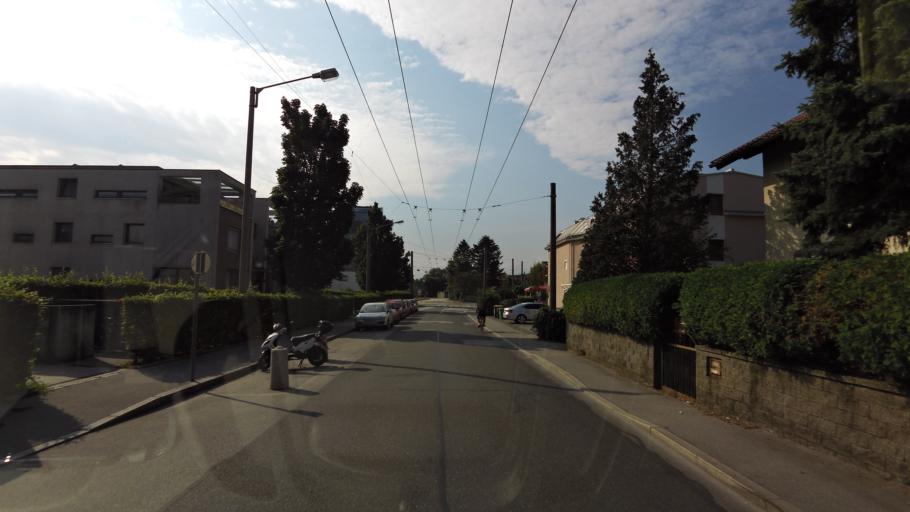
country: AT
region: Salzburg
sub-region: Politischer Bezirk Salzburg-Umgebung
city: Bergheim
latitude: 47.8296
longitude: 13.0224
